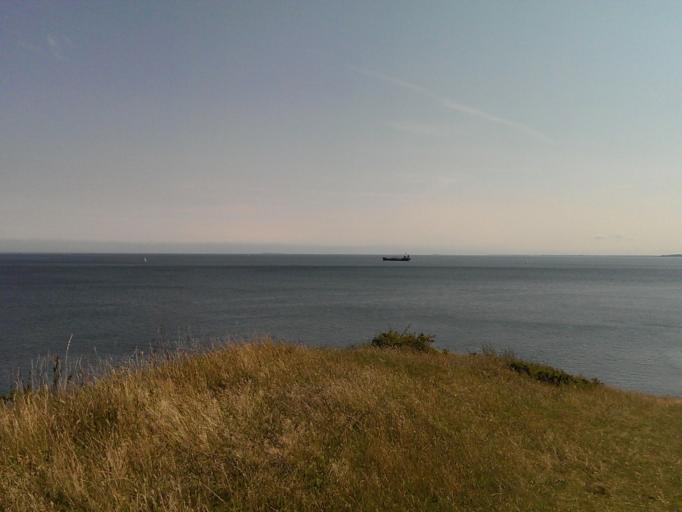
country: DK
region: Central Jutland
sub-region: Syddjurs Kommune
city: Ebeltoft
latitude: 56.1056
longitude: 10.5484
